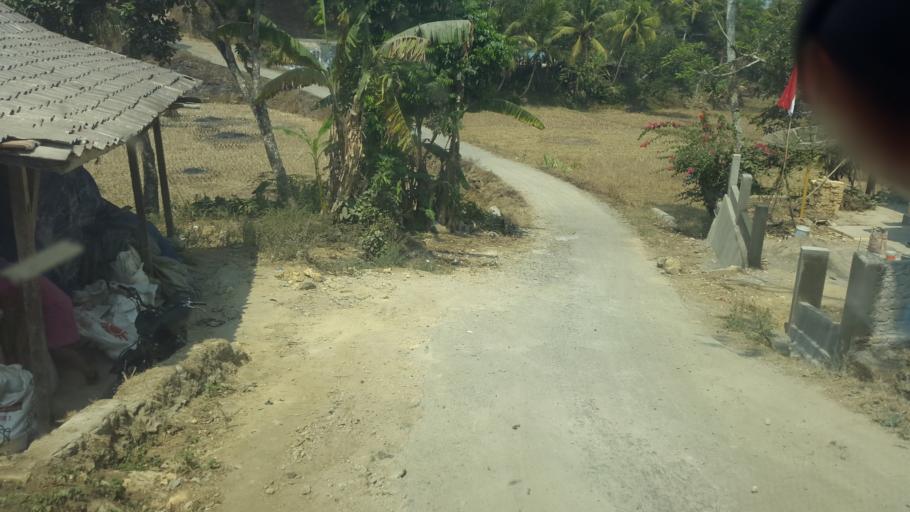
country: ID
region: West Java
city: Leuwinanggung Satu
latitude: -7.2967
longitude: 106.6447
